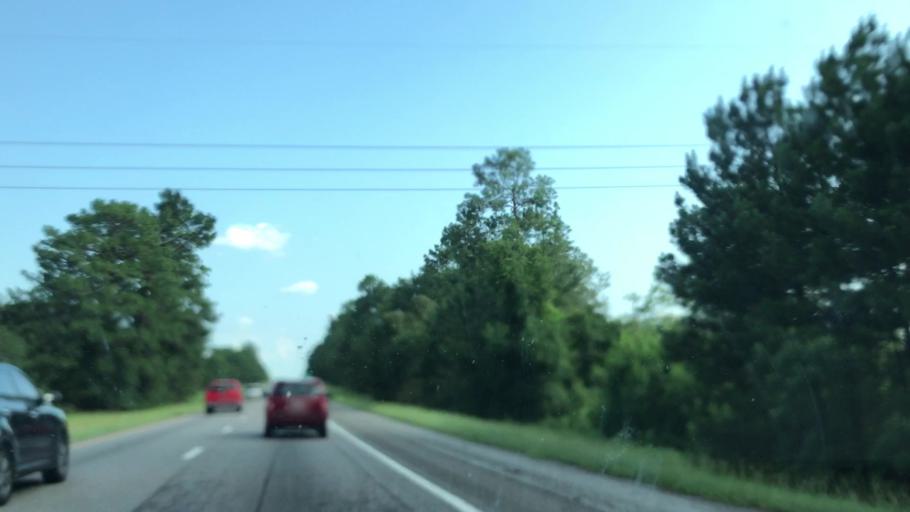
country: US
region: South Carolina
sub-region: Calhoun County
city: Saint Matthews
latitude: 33.6427
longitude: -80.8800
